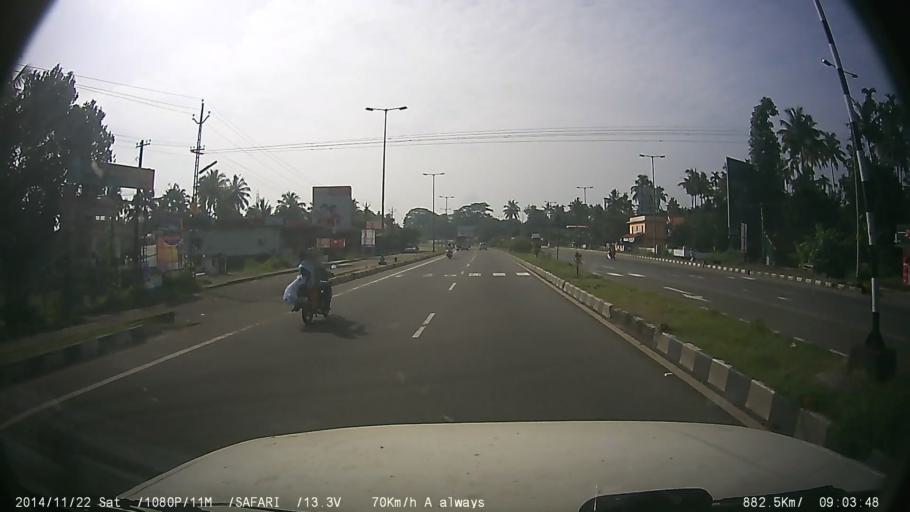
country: IN
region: Kerala
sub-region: Thrissur District
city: Kizhake Chalakudi
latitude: 10.3539
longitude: 76.3175
